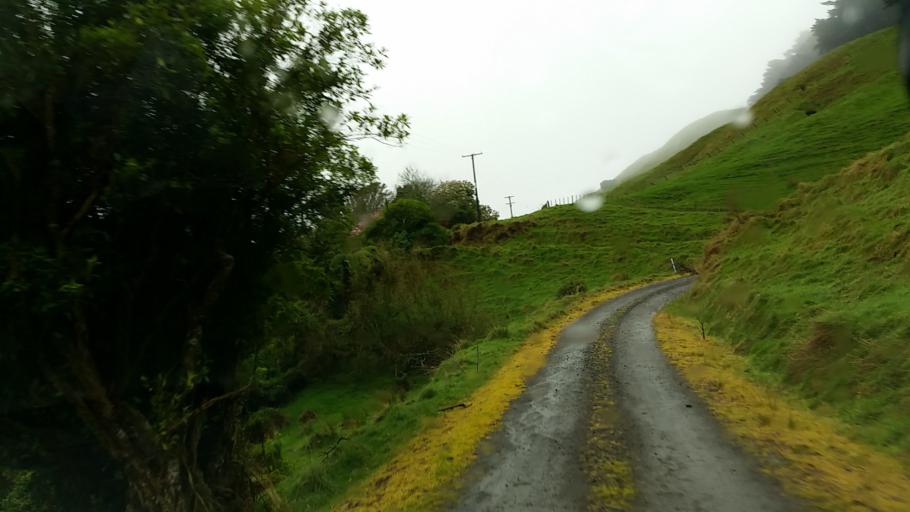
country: NZ
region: Taranaki
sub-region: South Taranaki District
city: Eltham
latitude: -39.4711
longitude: 174.4191
